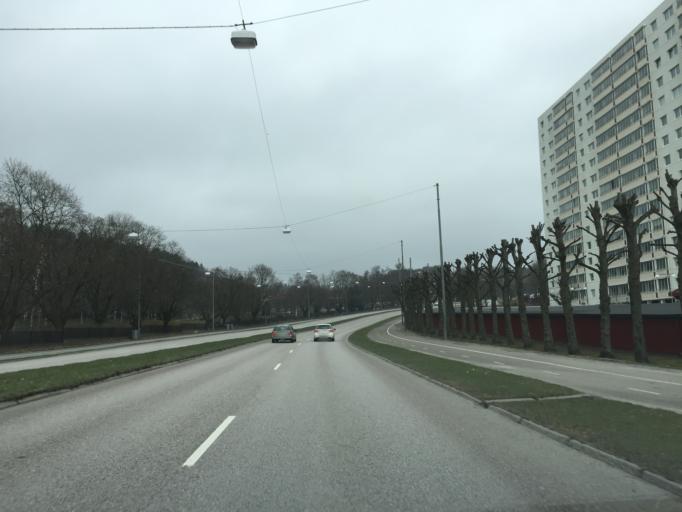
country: SE
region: Vaestra Goetaland
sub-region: Goteborg
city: Eriksbo
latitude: 57.7406
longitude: 12.0253
